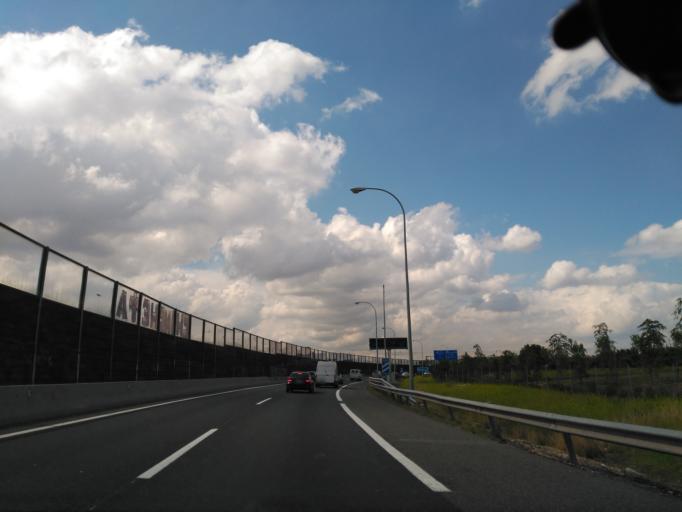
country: ES
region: Madrid
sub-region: Provincia de Madrid
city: Villaverde
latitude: 40.3547
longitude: -3.6787
